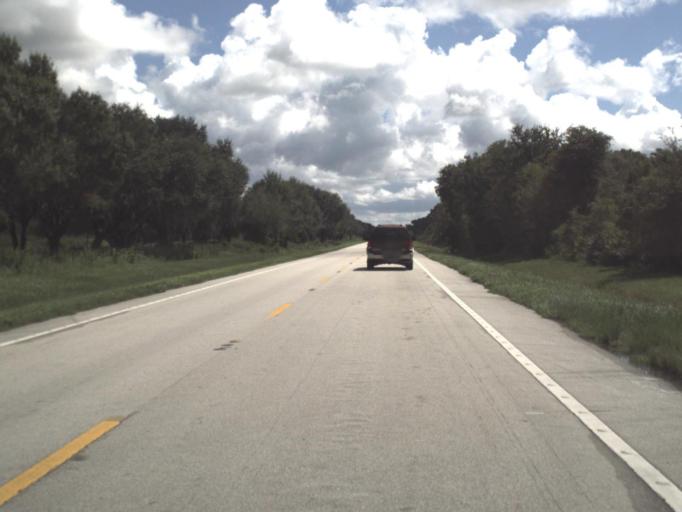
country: US
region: Florida
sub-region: DeSoto County
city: Arcadia
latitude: 27.2856
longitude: -82.0408
